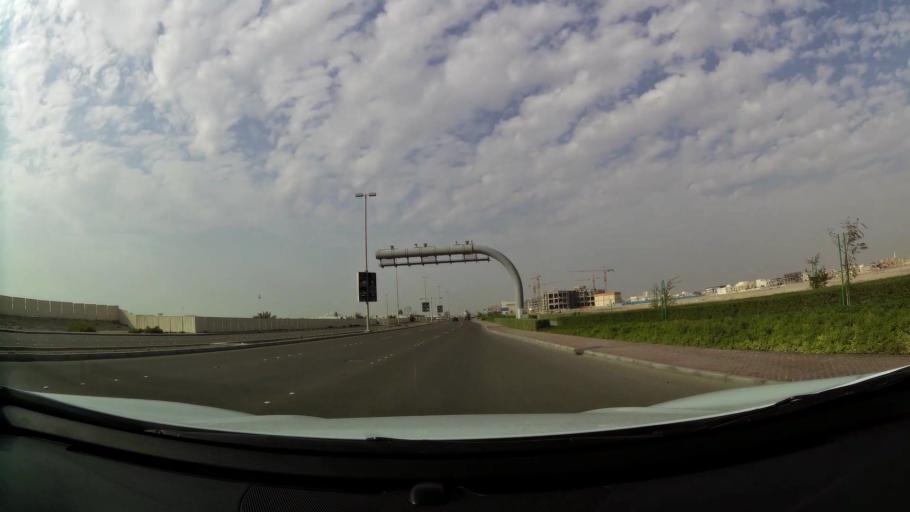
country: AE
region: Abu Dhabi
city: Abu Dhabi
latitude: 24.3482
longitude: 54.5377
